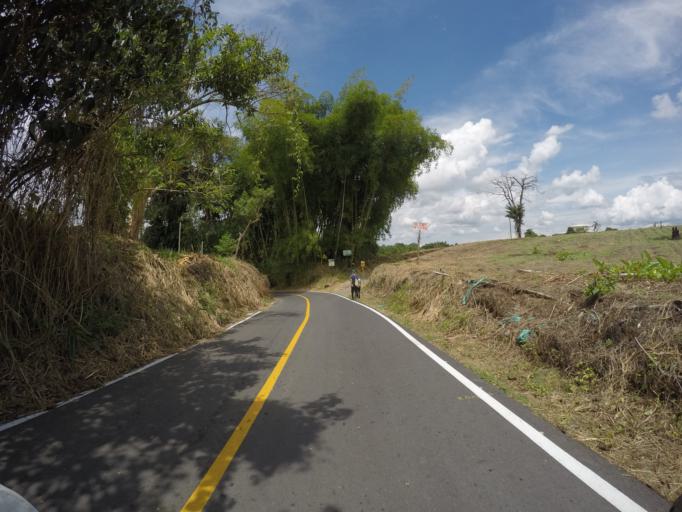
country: CO
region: Quindio
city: Quimbaya
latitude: 4.6153
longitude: -75.7620
